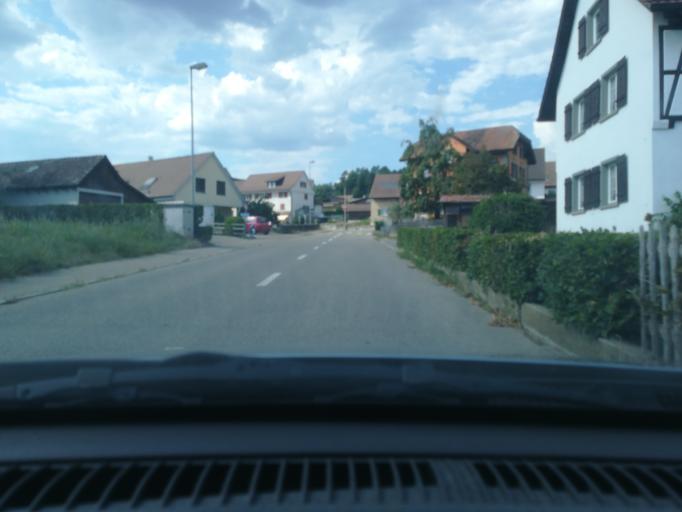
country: CH
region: Schaffhausen
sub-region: Bezirk Reiat
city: Thayngen
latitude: 47.7465
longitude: 8.7149
